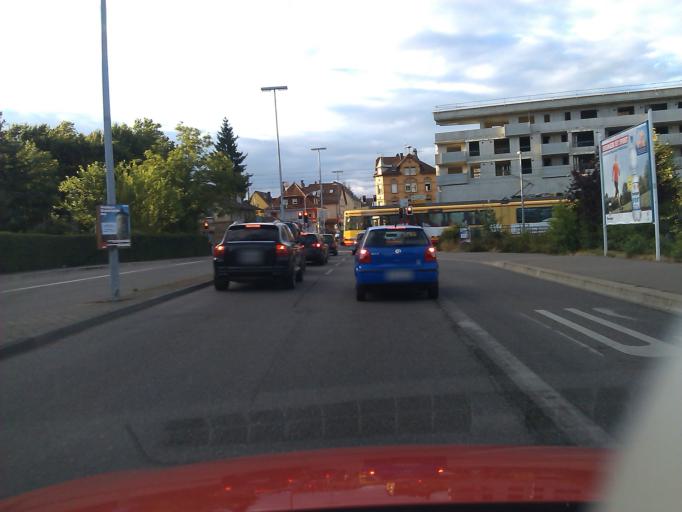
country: DE
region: Baden-Wuerttemberg
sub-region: Regierungsbezirk Stuttgart
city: Heilbronn
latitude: 49.1402
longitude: 9.1913
